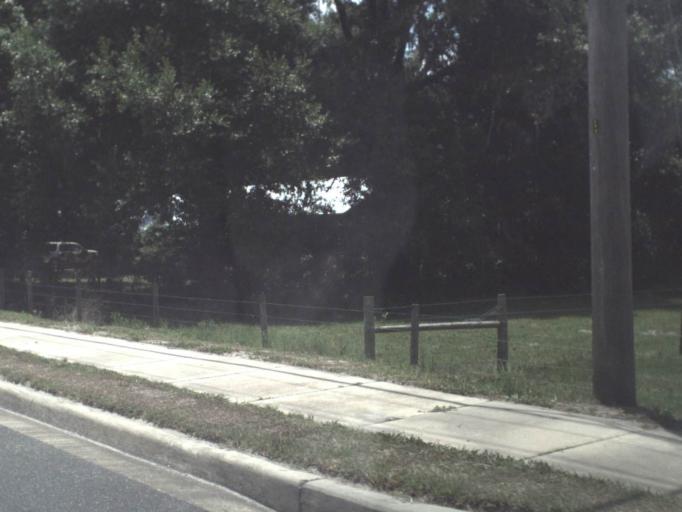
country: US
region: Florida
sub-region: Putnam County
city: Palatka
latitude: 29.6298
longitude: -81.7239
